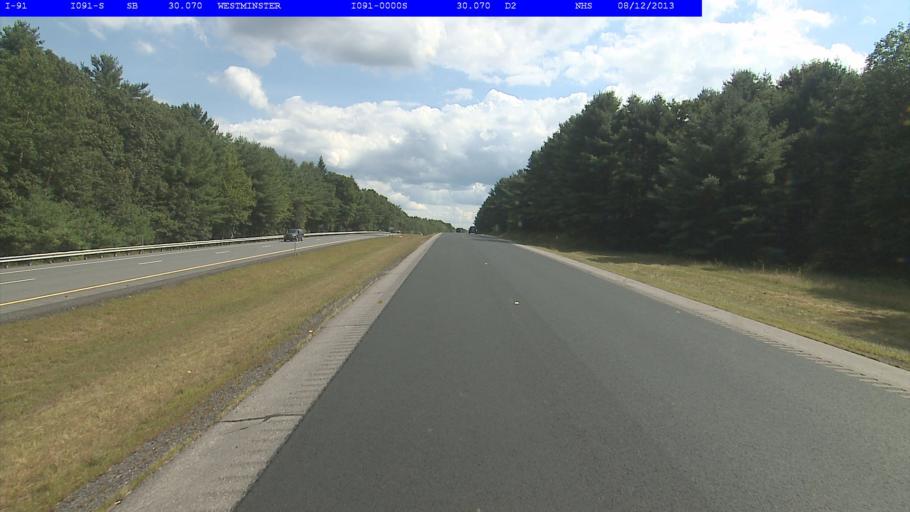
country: US
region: Vermont
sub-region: Windham County
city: Bellows Falls
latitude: 43.1116
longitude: -72.4579
